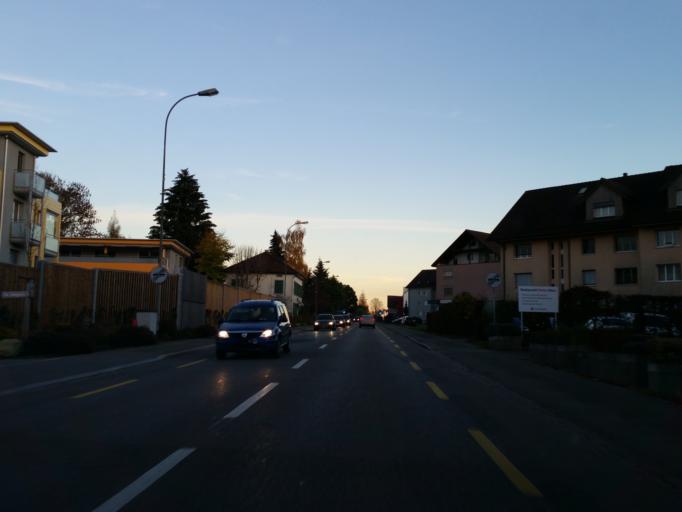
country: CH
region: Thurgau
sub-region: Kreuzlingen District
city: Munsterlingen
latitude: 47.6277
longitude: 9.2473
